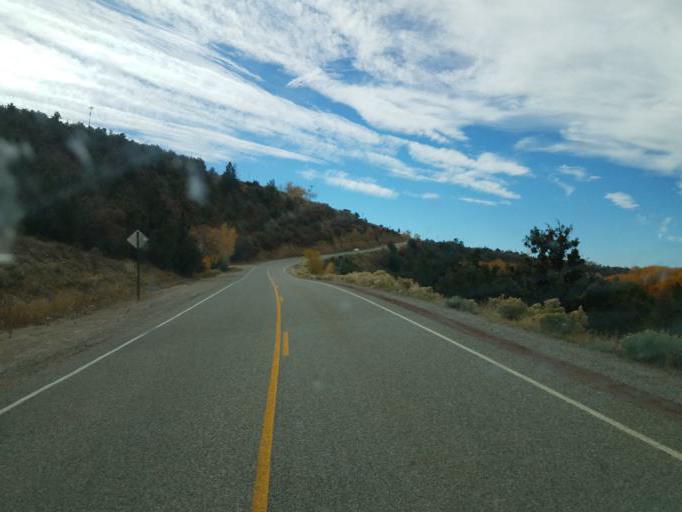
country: US
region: New Mexico
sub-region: Taos County
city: Arroyo Seco
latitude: 36.5367
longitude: -105.5612
